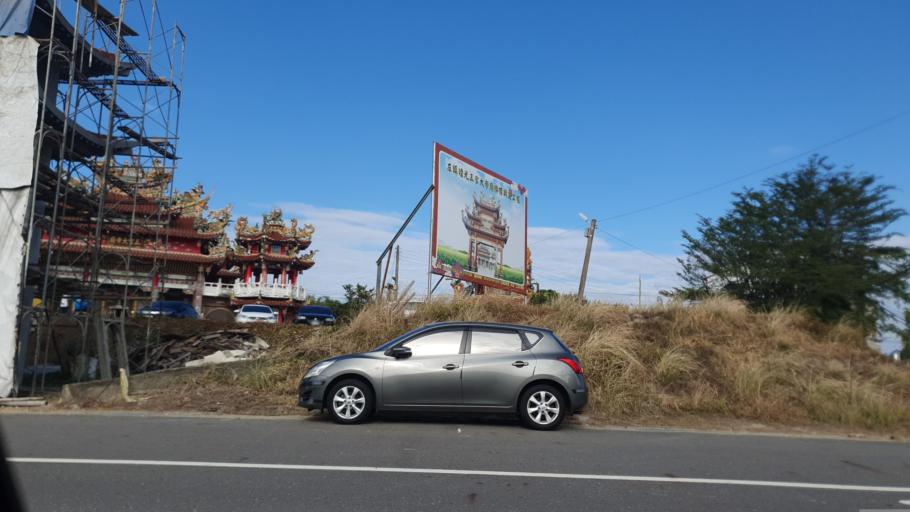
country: TW
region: Taiwan
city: Yujing
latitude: 23.0515
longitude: 120.4194
